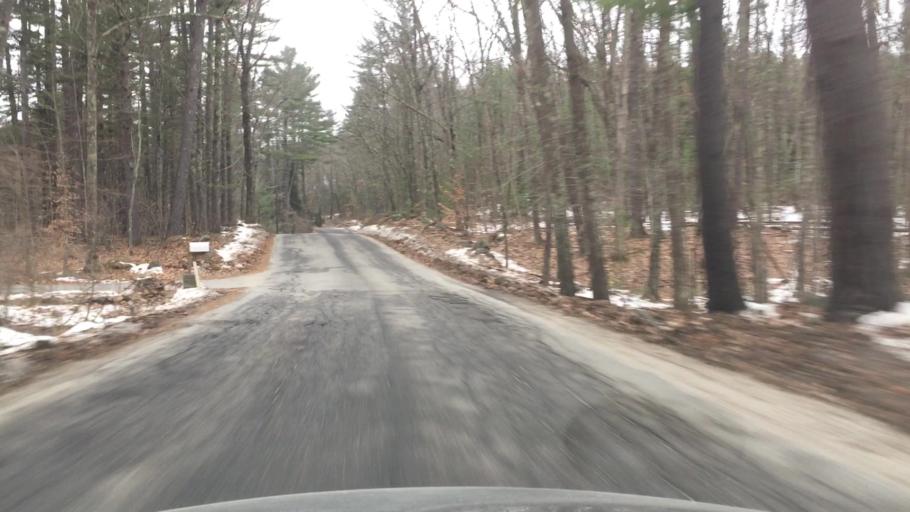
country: US
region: New Hampshire
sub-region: Hillsborough County
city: New Boston
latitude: 43.0082
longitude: -71.6695
